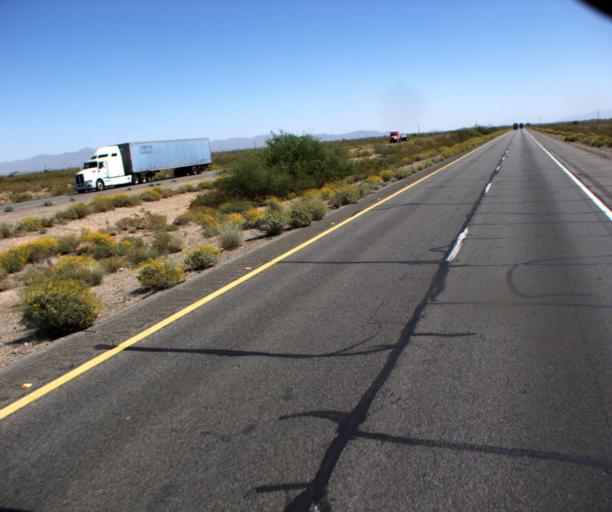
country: US
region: Arizona
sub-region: Maricopa County
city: Buckeye
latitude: 33.4764
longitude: -112.8438
